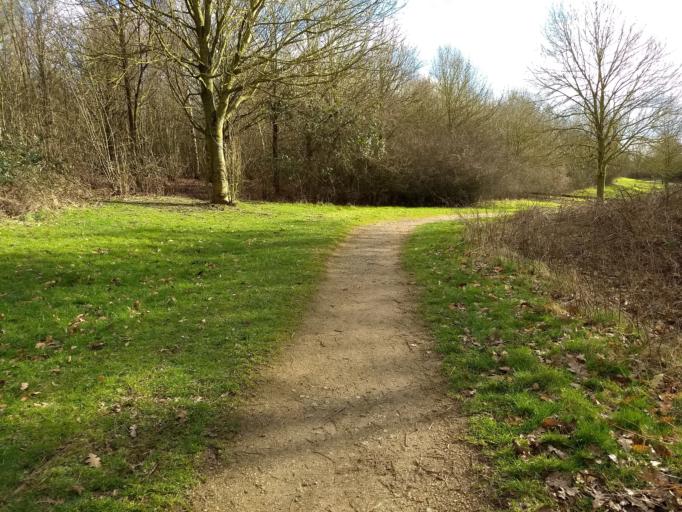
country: GB
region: England
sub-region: Buckinghamshire
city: Bletchley
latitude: 51.9851
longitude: -0.7343
